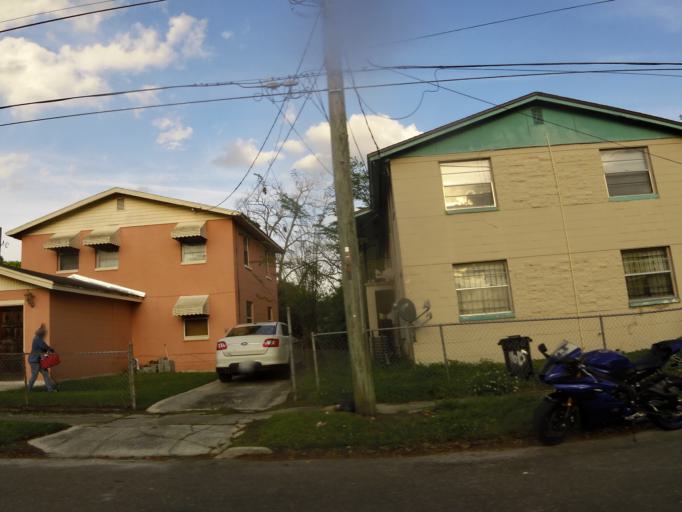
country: US
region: Florida
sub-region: Duval County
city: Jacksonville
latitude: 30.3446
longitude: -81.6820
